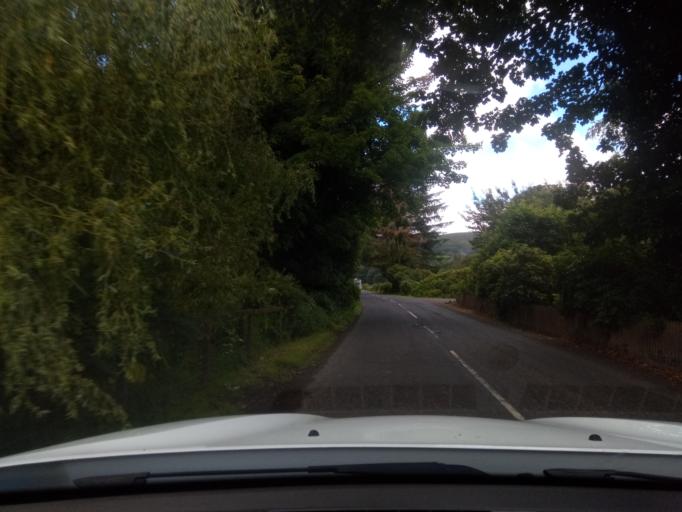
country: GB
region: Scotland
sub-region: The Scottish Borders
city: Selkirk
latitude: 55.5597
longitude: -2.9399
